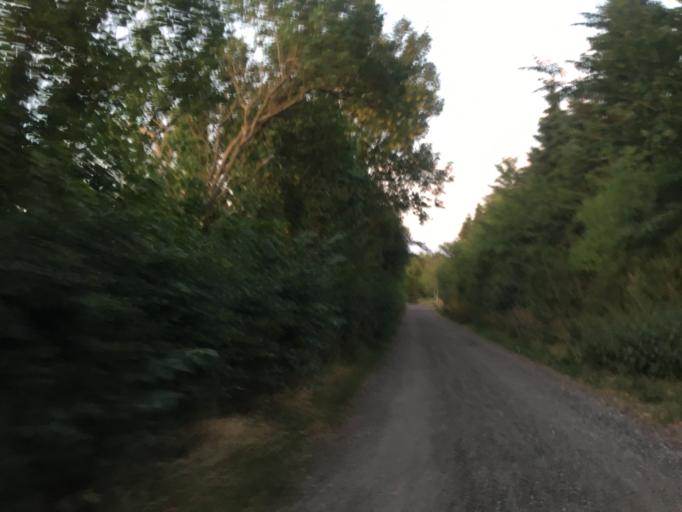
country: DK
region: Central Jutland
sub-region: Syddjurs Kommune
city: Hornslet
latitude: 56.3176
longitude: 10.3271
